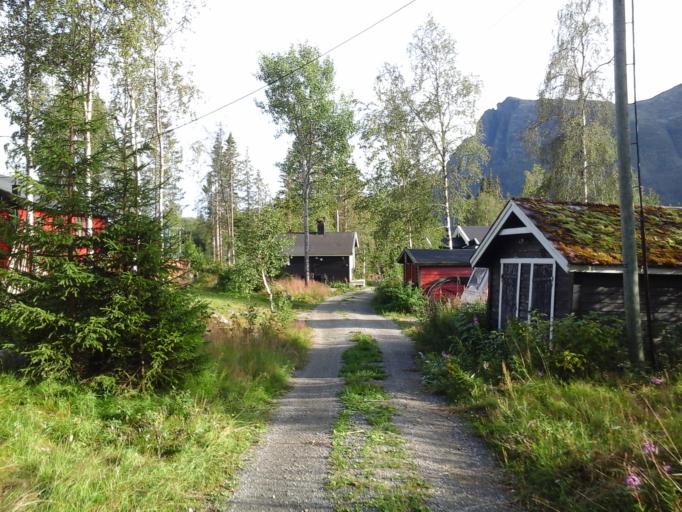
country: NO
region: Buskerud
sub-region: Hemsedal
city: Troim
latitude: 60.8441
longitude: 8.6190
